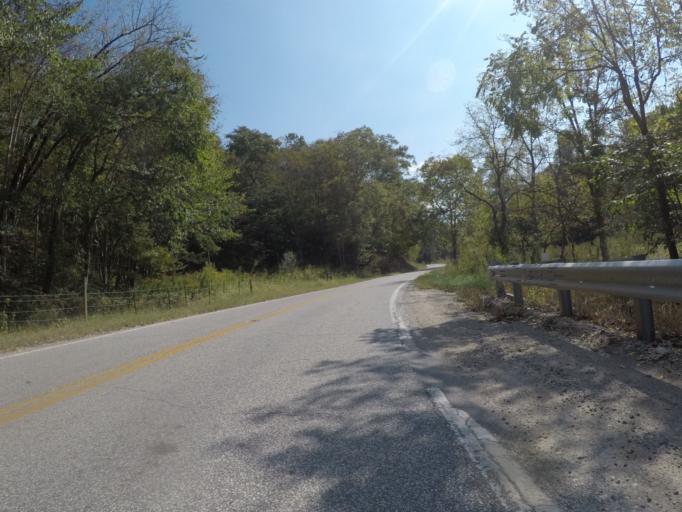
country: US
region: West Virginia
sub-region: Cabell County
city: Lesage
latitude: 38.5791
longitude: -82.4130
